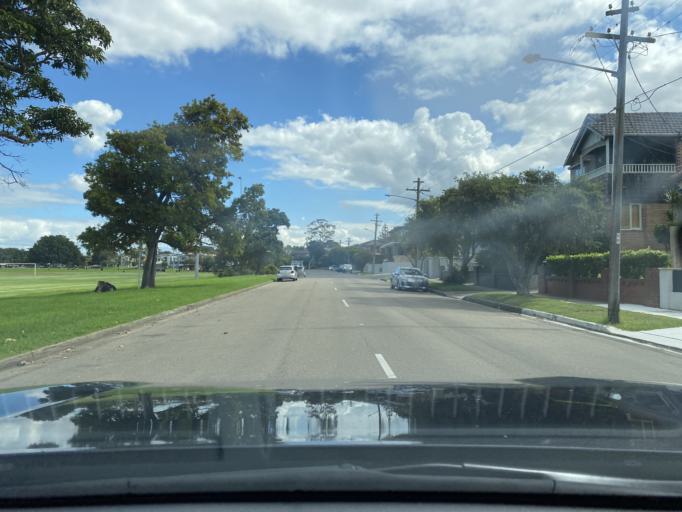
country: AU
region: New South Wales
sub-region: Canada Bay
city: Wareemba
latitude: -33.8686
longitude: 151.1401
